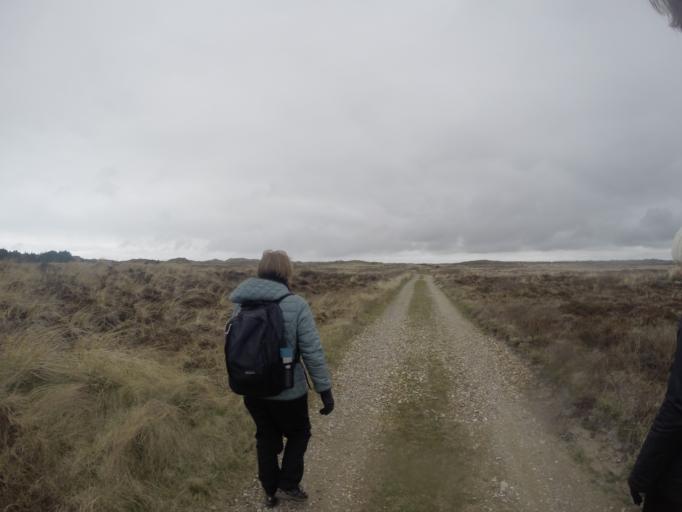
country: DK
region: North Denmark
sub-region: Thisted Kommune
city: Hurup
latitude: 56.8912
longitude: 8.3273
